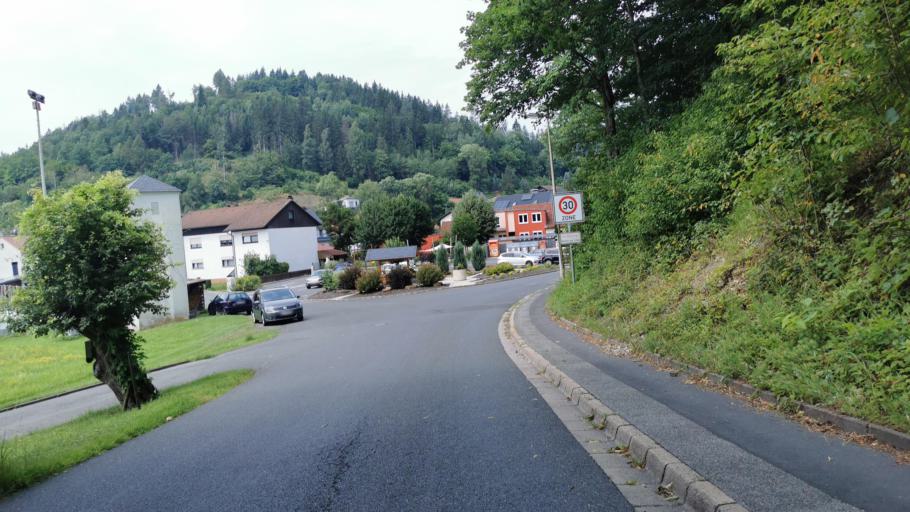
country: DE
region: Bavaria
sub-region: Upper Franconia
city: Wilhelmsthal
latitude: 50.2792
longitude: 11.3682
